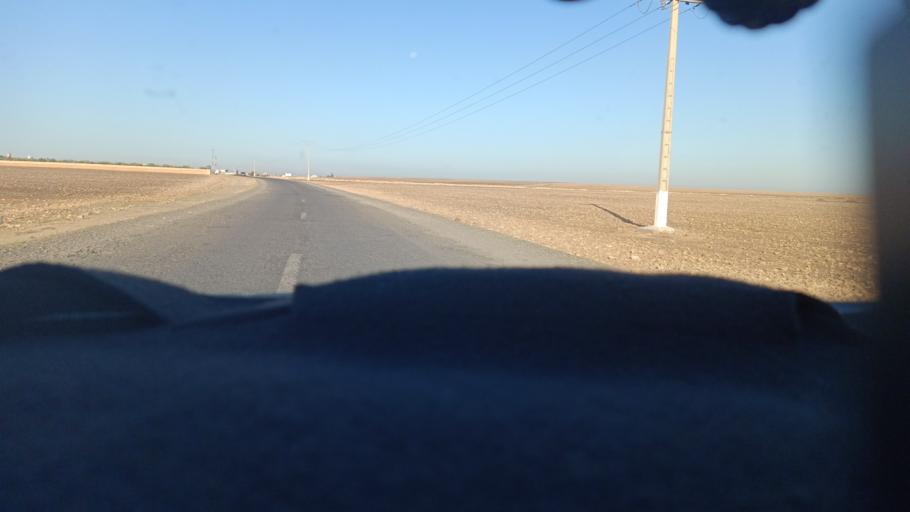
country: MA
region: Doukkala-Abda
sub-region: Safi
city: Youssoufia
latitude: 32.3710
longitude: -8.6642
